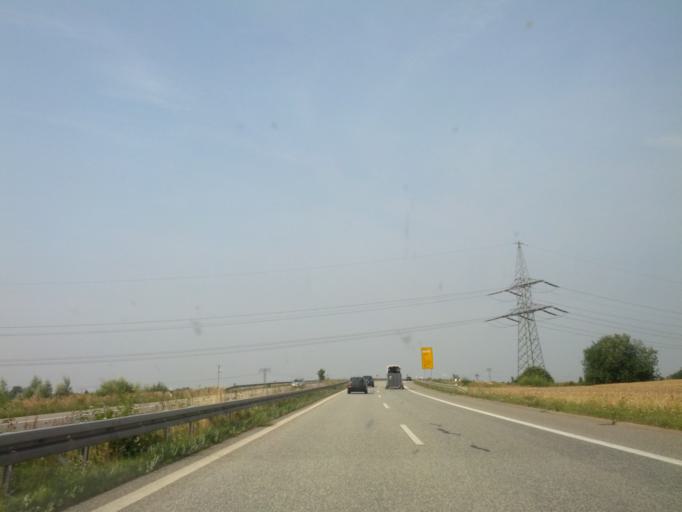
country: DE
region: Mecklenburg-Vorpommern
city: Wendorf
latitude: 54.2802
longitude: 13.0761
